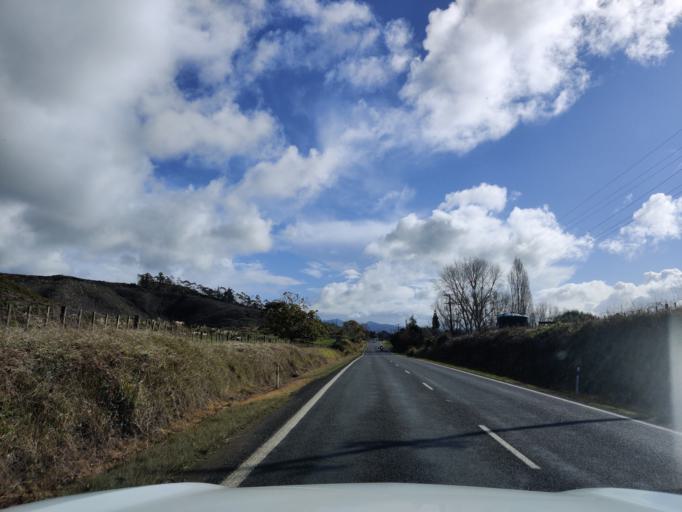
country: NZ
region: Waikato
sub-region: Thames-Coromandel District
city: Whitianga
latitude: -36.7493
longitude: 175.6809
